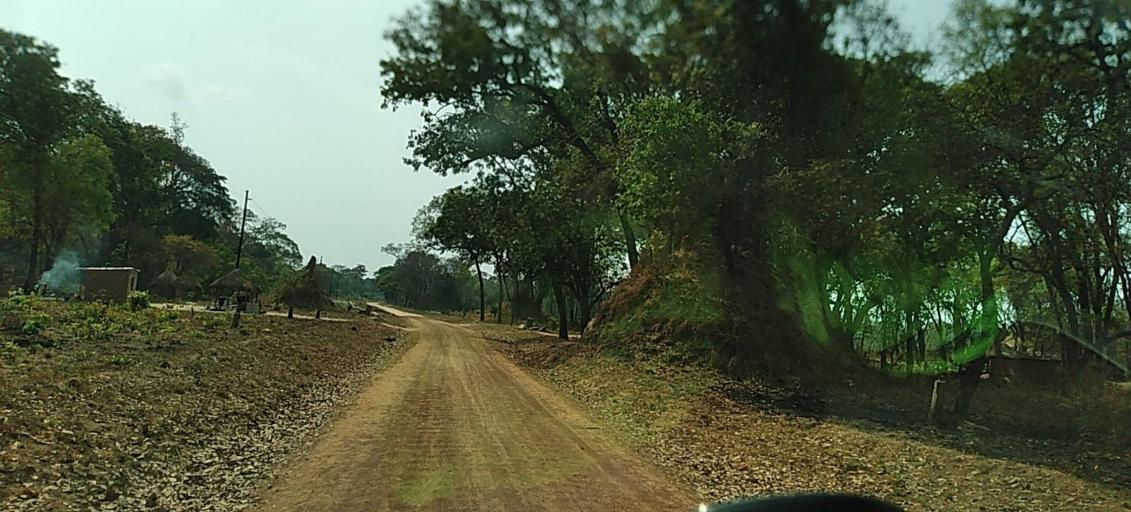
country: ZM
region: North-Western
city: Solwezi
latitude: -12.7090
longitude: 26.4213
